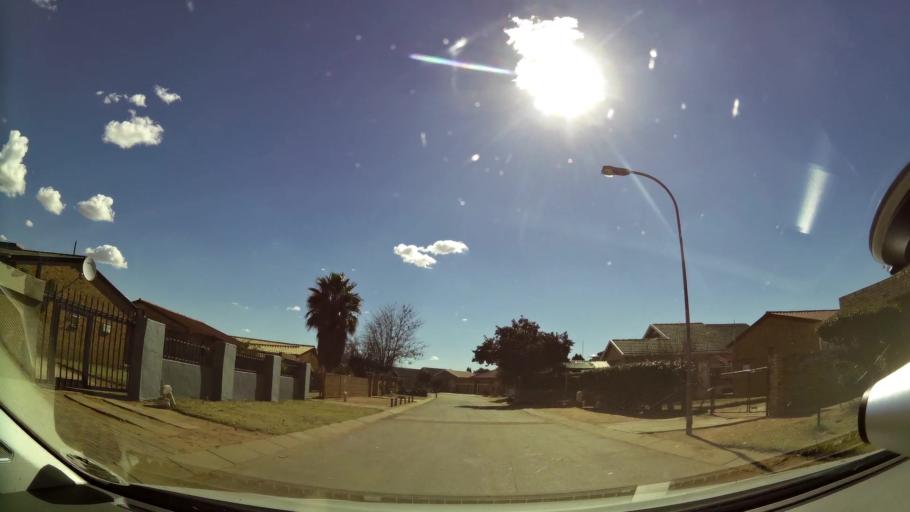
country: ZA
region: North-West
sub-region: Dr Kenneth Kaunda District Municipality
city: Klerksdorp
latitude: -26.8705
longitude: 26.5846
